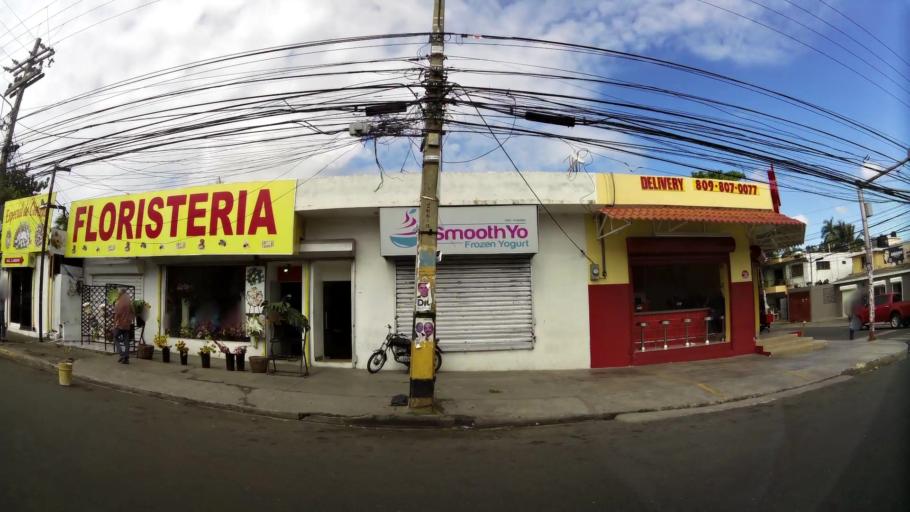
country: DO
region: Santo Domingo
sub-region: Santo Domingo
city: Santo Domingo Este
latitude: 18.4921
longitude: -69.8652
